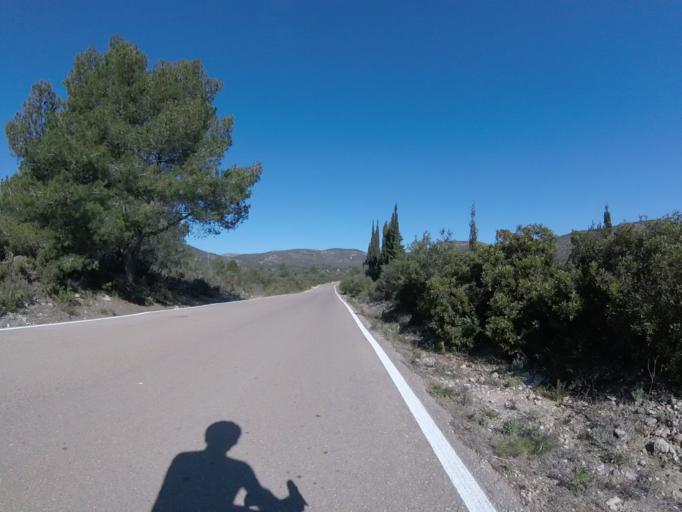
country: ES
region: Valencia
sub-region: Provincia de Castello
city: Santa Magdalena de Pulpis
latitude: 40.3683
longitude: 0.2750
